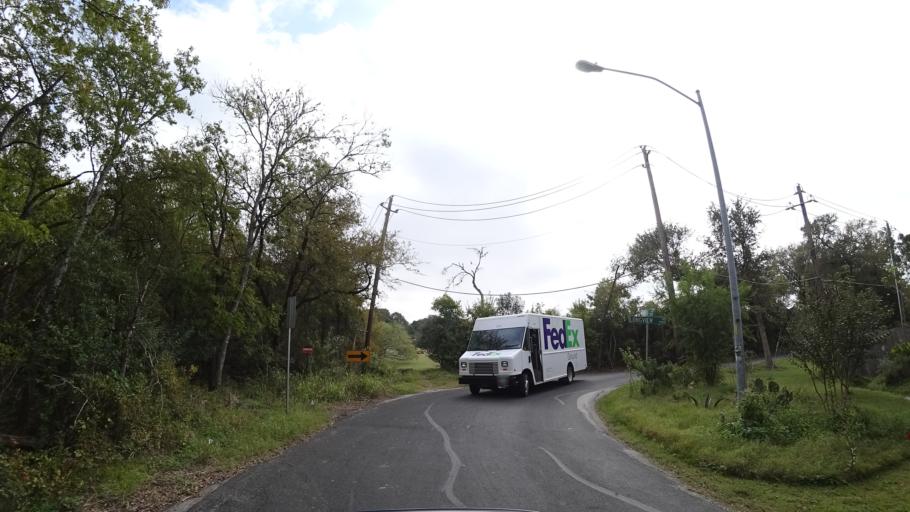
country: US
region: Texas
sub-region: Travis County
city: Shady Hollow
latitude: 30.2047
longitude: -97.8264
